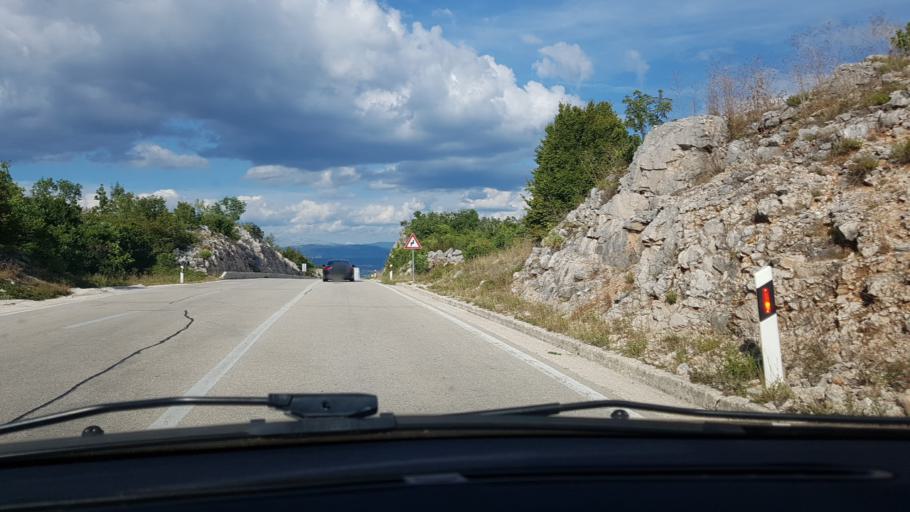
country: HR
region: Splitsko-Dalmatinska
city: Grubine
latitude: 43.4171
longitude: 17.0990
